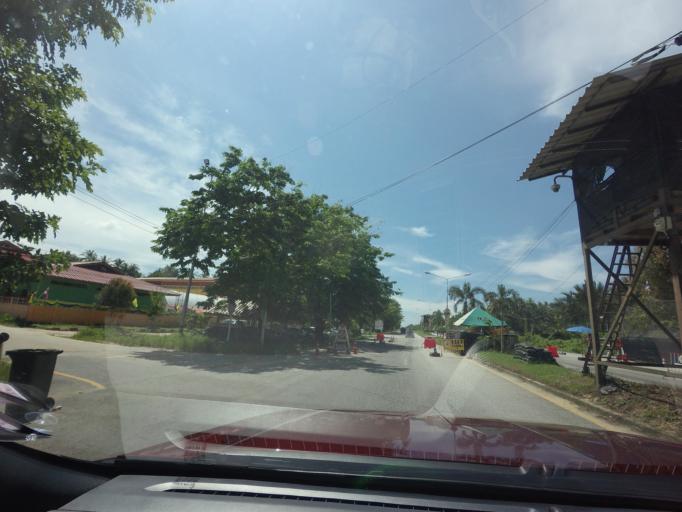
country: TH
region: Pattani
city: Mai Kaen
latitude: 6.6163
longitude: 101.6299
